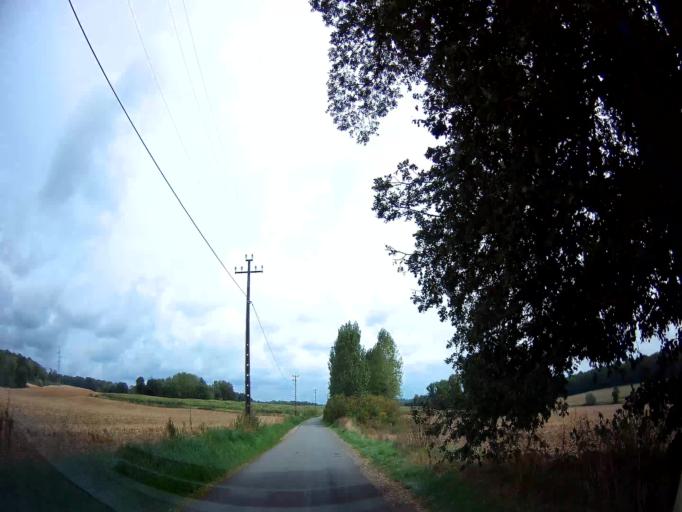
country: BE
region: Wallonia
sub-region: Province de Namur
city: Havelange
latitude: 50.4194
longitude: 5.1990
